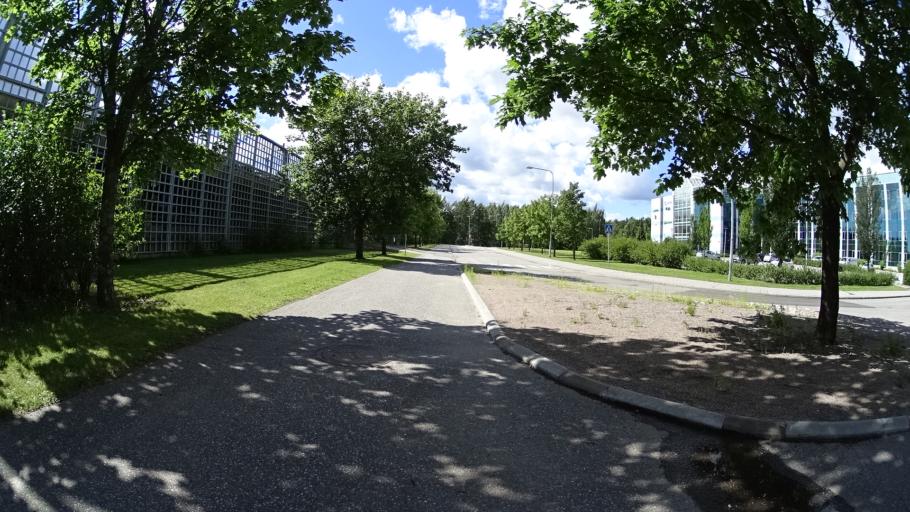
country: FI
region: Uusimaa
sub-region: Helsinki
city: Teekkarikylae
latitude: 60.2843
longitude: 24.8535
